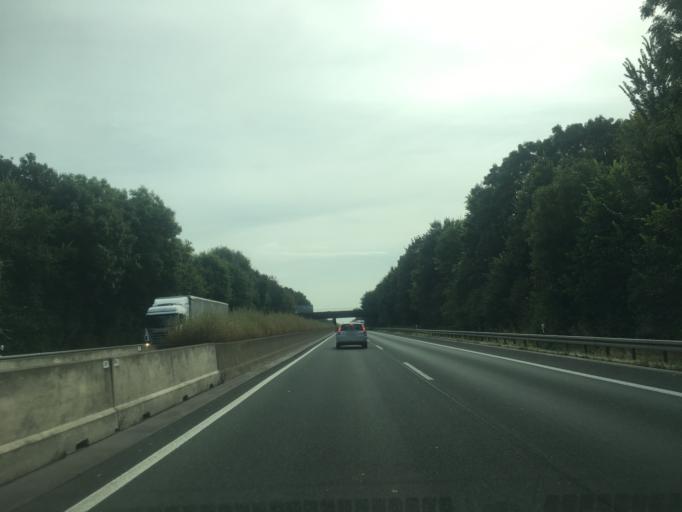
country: DE
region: North Rhine-Westphalia
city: Tuernich
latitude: 50.8385
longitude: 6.7593
